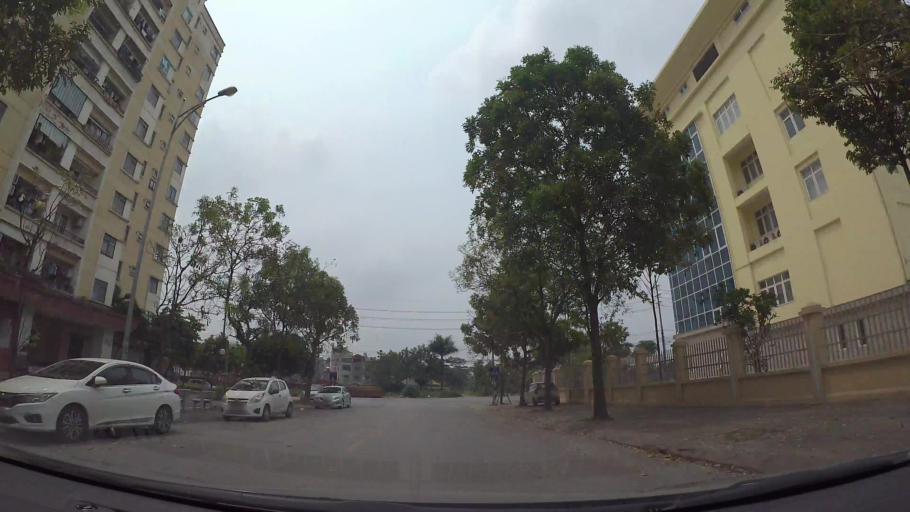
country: VN
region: Ha Noi
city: Trau Quy
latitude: 21.0686
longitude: 105.9092
